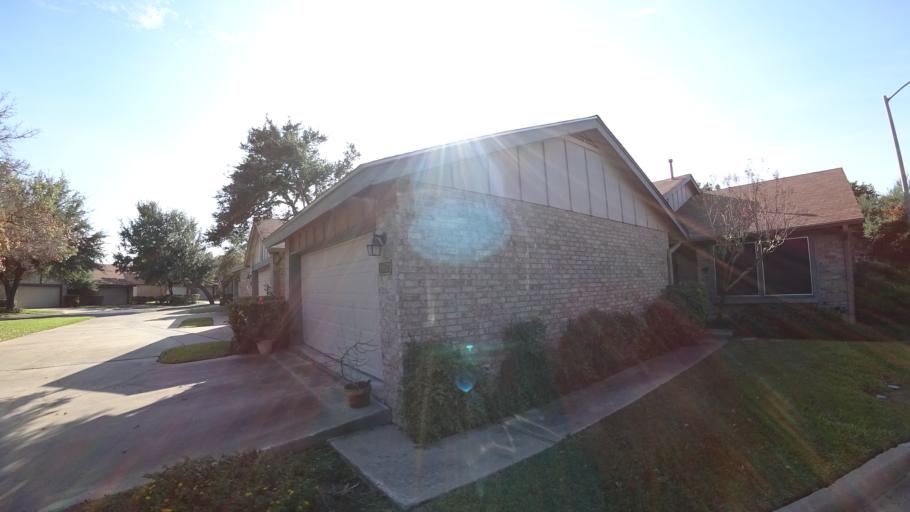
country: US
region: Texas
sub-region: Williamson County
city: Anderson Mill
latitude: 30.4550
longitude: -97.8083
